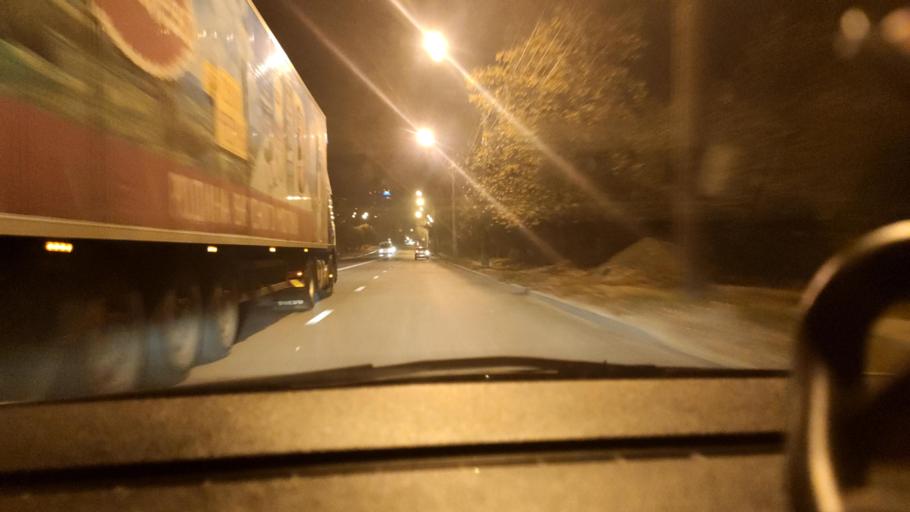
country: RU
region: Voronezj
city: Voronezh
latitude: 51.6947
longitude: 39.1713
